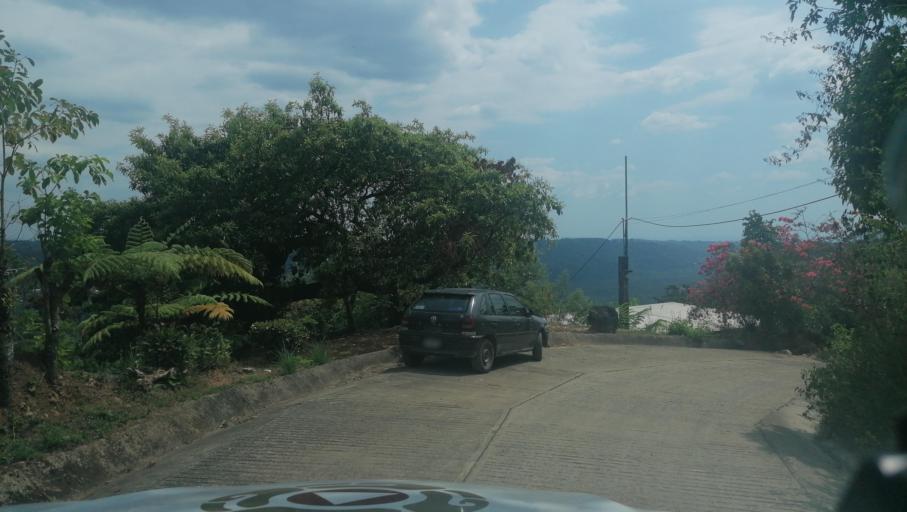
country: MX
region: Chiapas
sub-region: Cacahoatan
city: Benito Juarez
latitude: 15.0587
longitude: -92.2266
